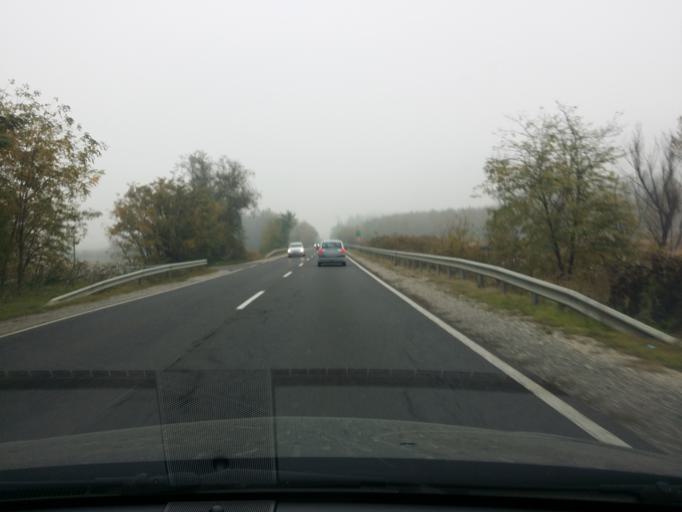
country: HU
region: Szabolcs-Szatmar-Bereg
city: Nyirbogdany
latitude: 48.0327
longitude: 21.8545
